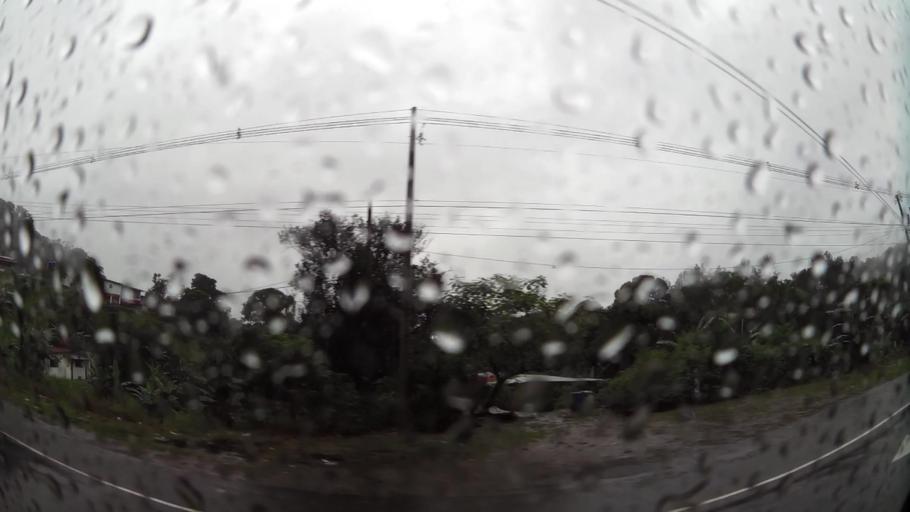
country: PA
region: Colon
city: Gatun
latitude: 9.2922
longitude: -79.7485
